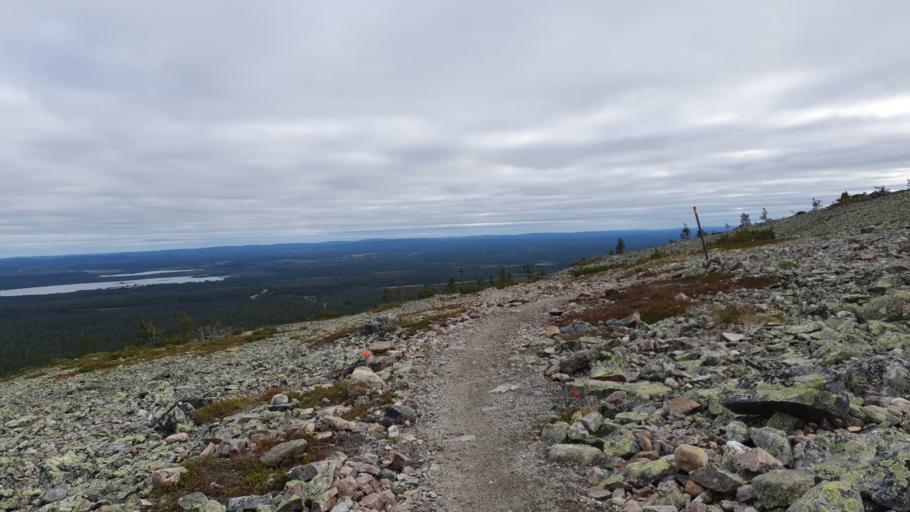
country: FI
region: Lapland
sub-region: Tunturi-Lappi
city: Kolari
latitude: 67.5649
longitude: 24.2512
